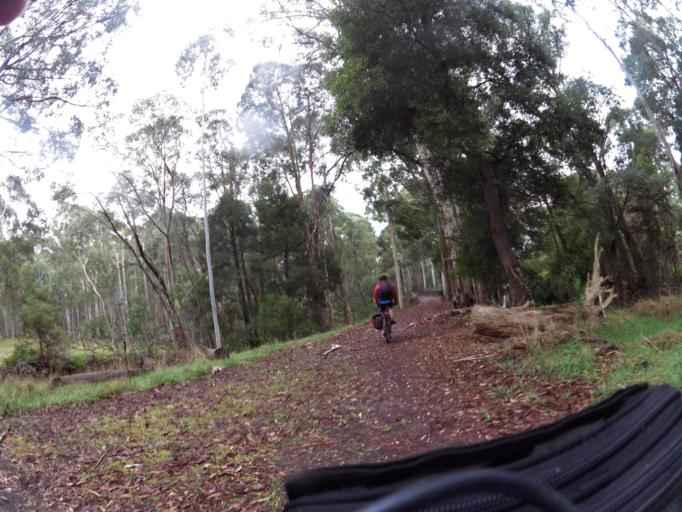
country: AU
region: New South Wales
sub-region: Greater Hume Shire
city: Holbrook
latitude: -36.1617
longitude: 147.4867
